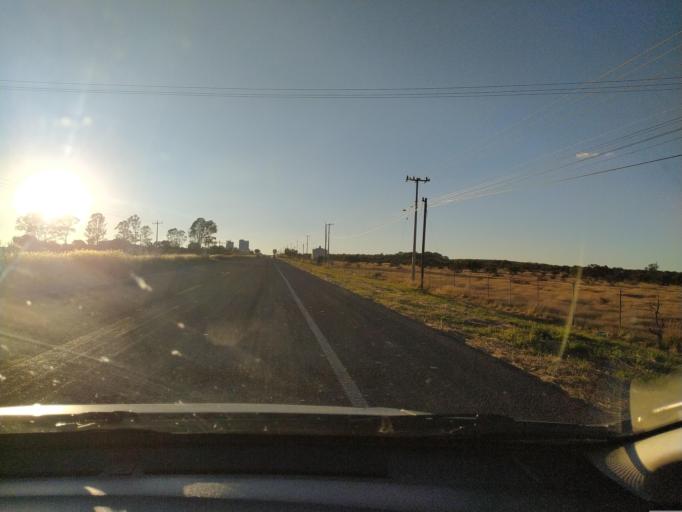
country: MX
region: Jalisco
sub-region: San Julian
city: Colonia Veintitres de Mayo
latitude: 21.0117
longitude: -102.2105
